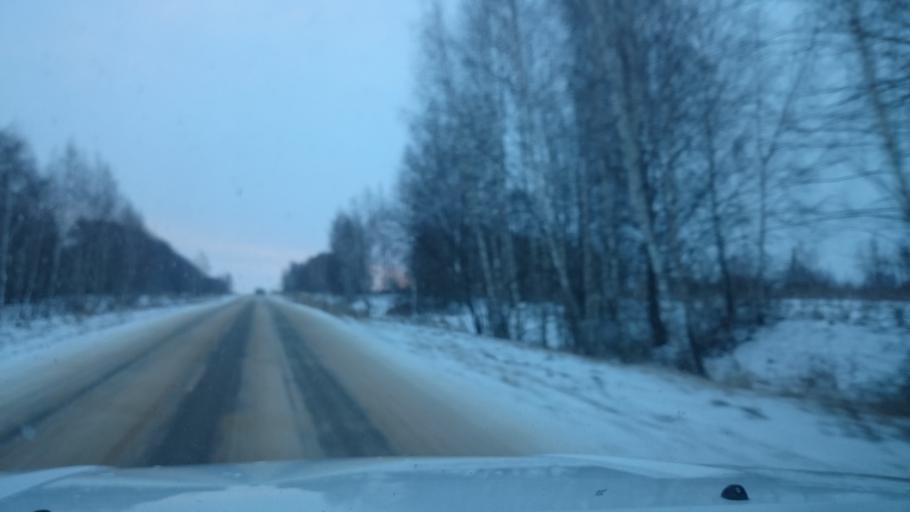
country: RU
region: Tula
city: Leninskiy
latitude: 54.2439
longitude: 37.2728
